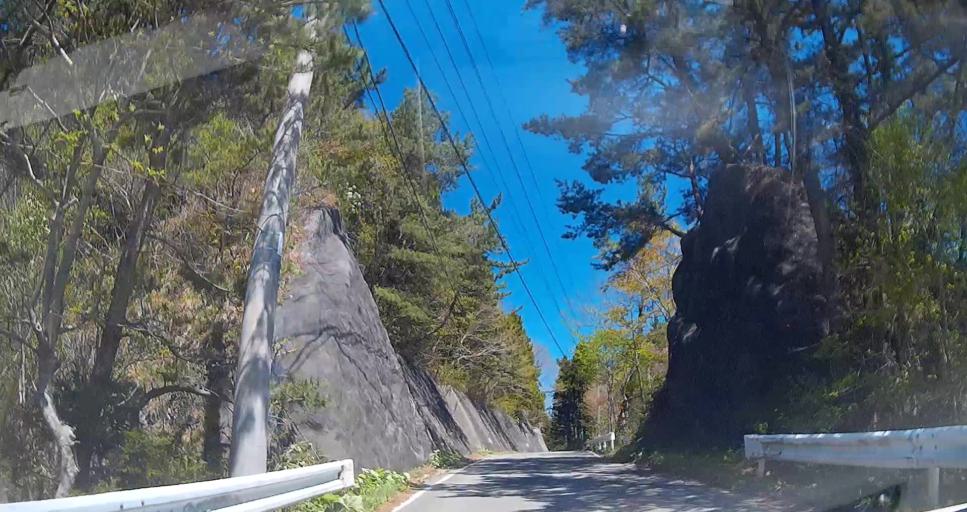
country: JP
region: Aomori
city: Mutsu
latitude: 41.1189
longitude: 141.3916
